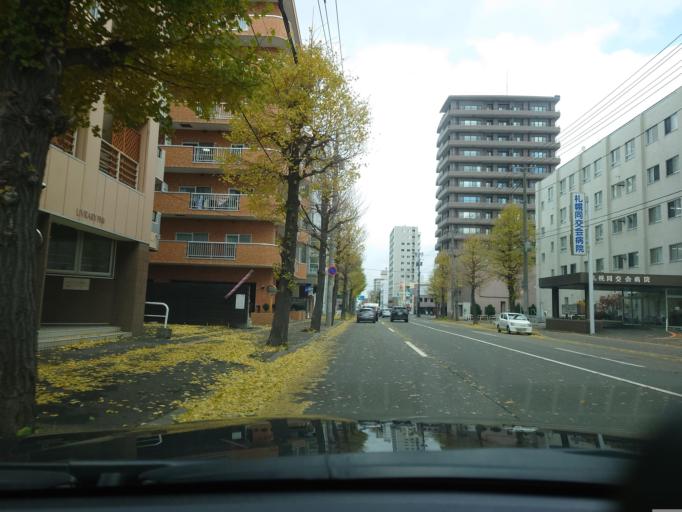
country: JP
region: Hokkaido
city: Sapporo
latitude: 43.0544
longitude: 141.3278
